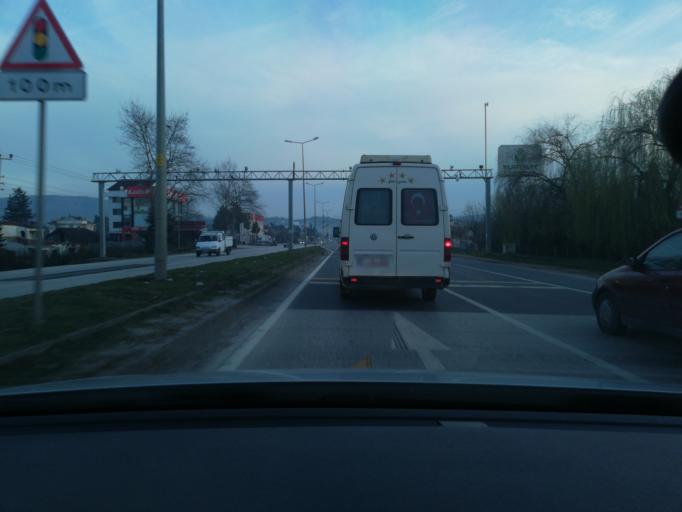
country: TR
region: Duzce
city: Duzce
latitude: 40.8748
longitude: 31.1695
